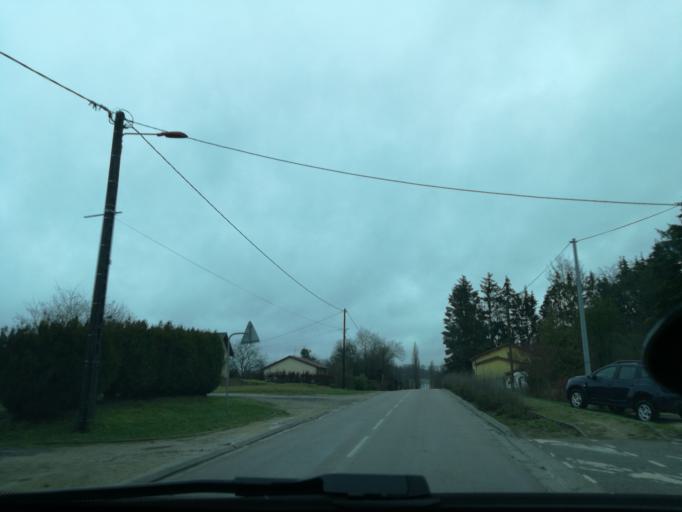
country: FR
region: Lorraine
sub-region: Departement de la Meuse
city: Clermont-en-Argonne
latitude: 49.0586
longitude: 5.1205
